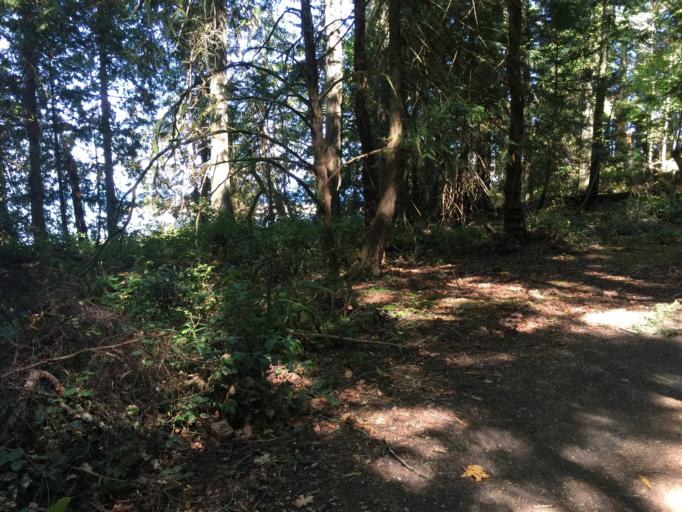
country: CA
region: British Columbia
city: Nanaimo
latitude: 49.1931
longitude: -123.9263
